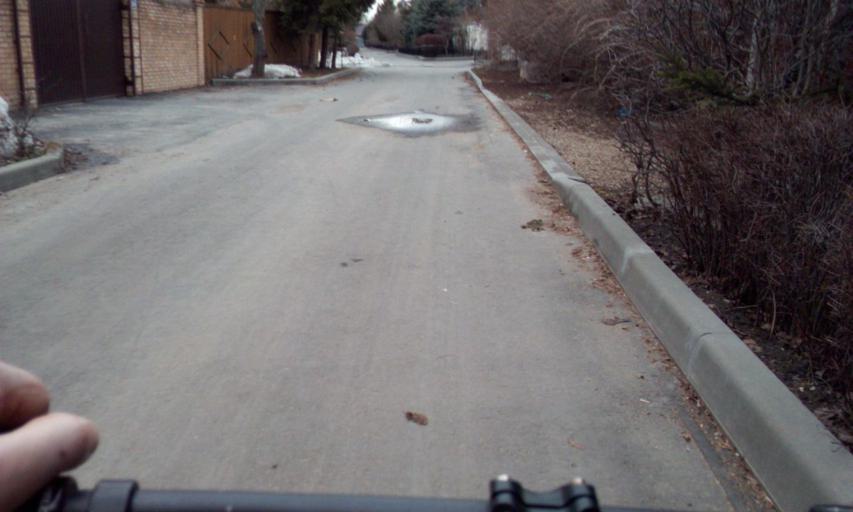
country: RU
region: Moskovskaya
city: Filimonki
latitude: 55.5222
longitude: 37.3687
